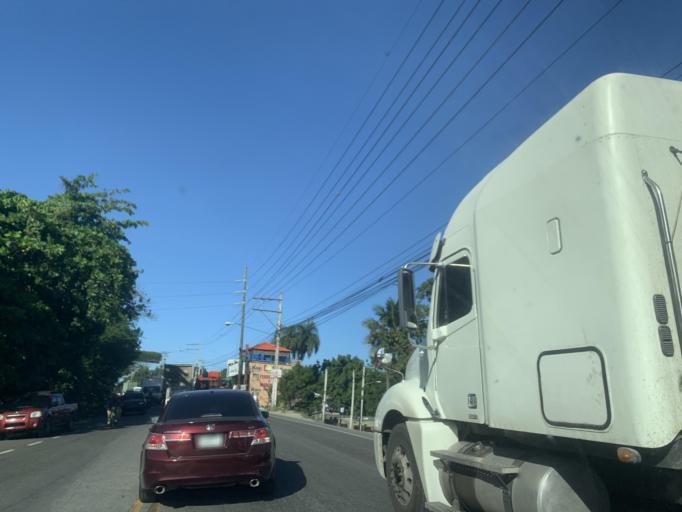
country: DO
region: San Cristobal
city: Bajos de Haina
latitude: 18.4258
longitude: -70.0376
